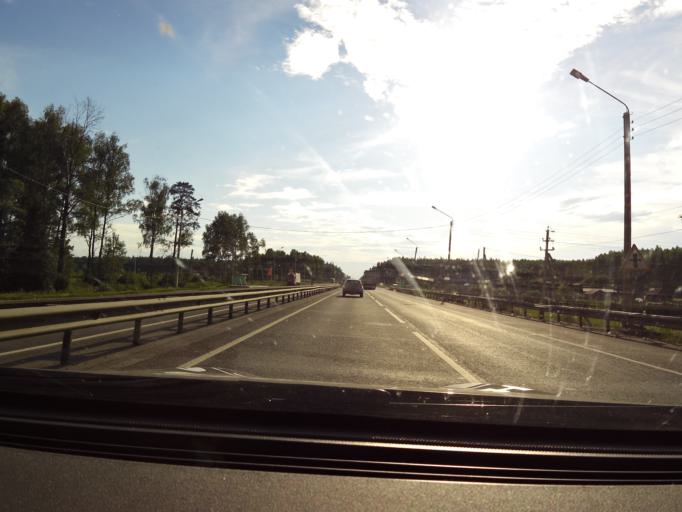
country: RU
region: Vladimir
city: Krasnyy Oktyabr'
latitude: 56.2170
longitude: 41.4259
